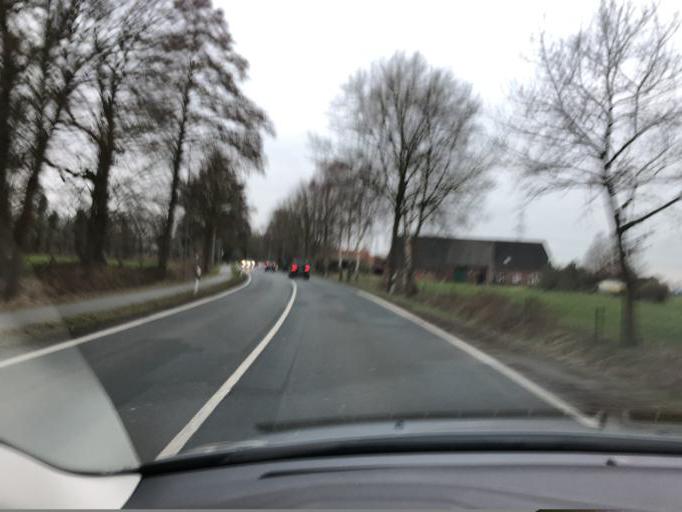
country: DE
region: Lower Saxony
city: Ganderkesee
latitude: 53.0646
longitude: 8.5740
